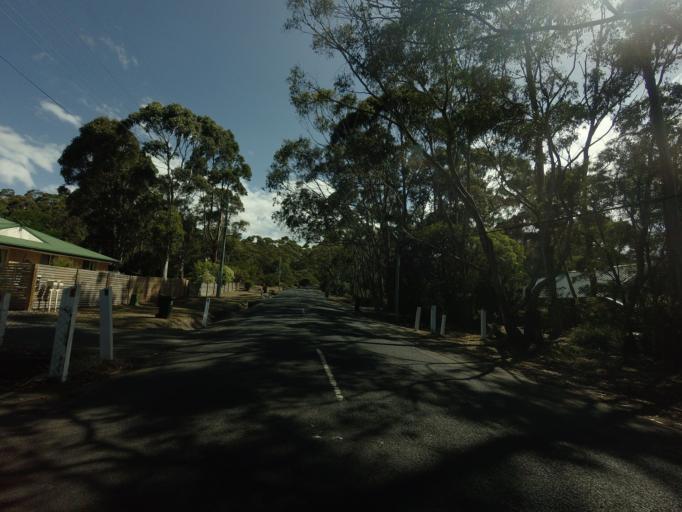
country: AU
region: Tasmania
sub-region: Kingborough
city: Taroona
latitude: -42.9265
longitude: 147.3377
